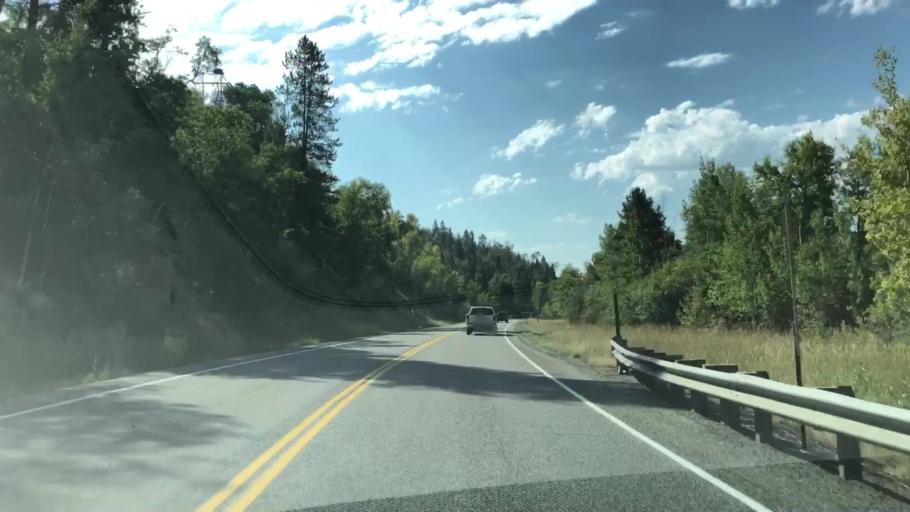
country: US
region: Idaho
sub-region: Teton County
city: Victor
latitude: 43.2770
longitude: -111.1146
